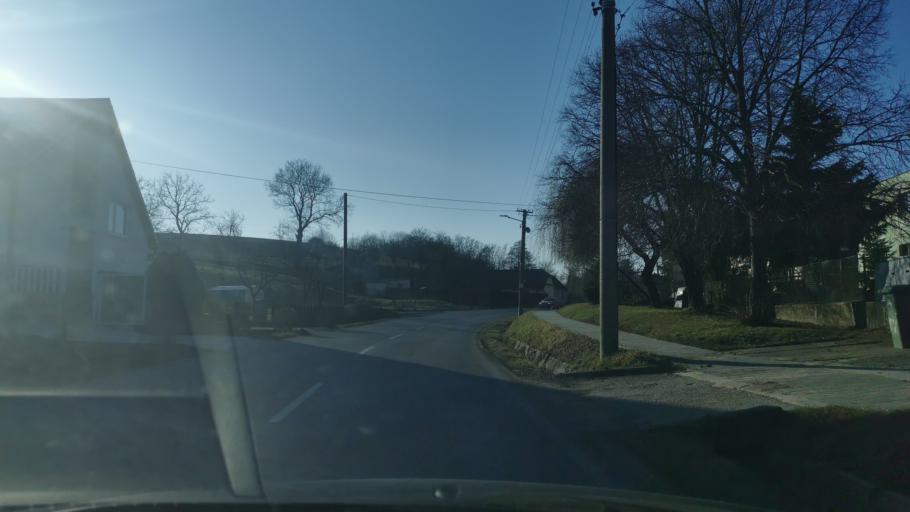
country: SK
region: Trnavsky
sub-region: Okres Senica
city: Senica
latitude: 48.7302
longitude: 17.4029
